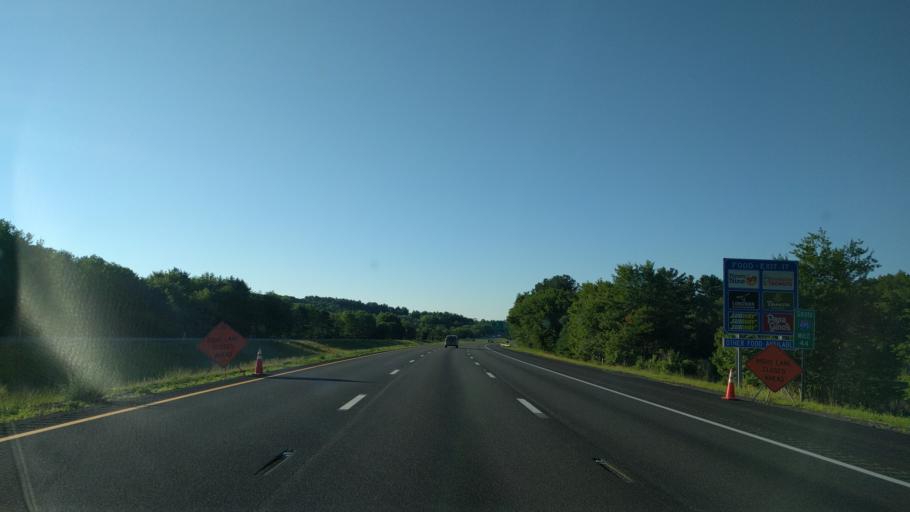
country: US
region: Massachusetts
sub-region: Norfolk County
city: Bellingham
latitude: 42.0991
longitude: -71.4380
